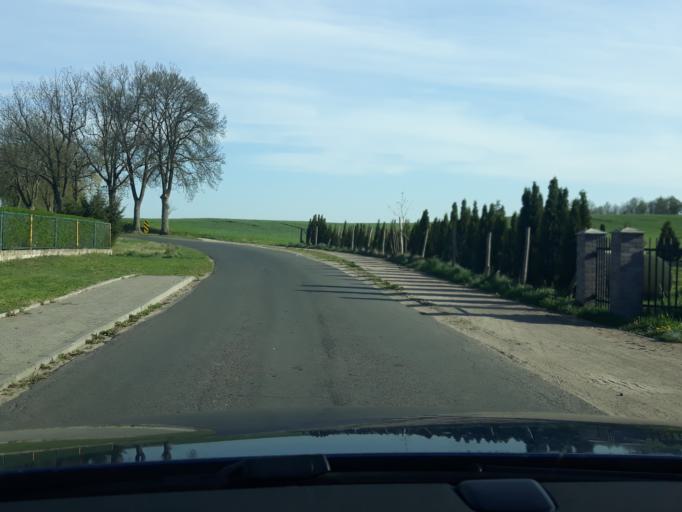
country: PL
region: Pomeranian Voivodeship
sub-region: Powiat czluchowski
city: Przechlewo
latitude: 53.8407
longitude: 17.3619
